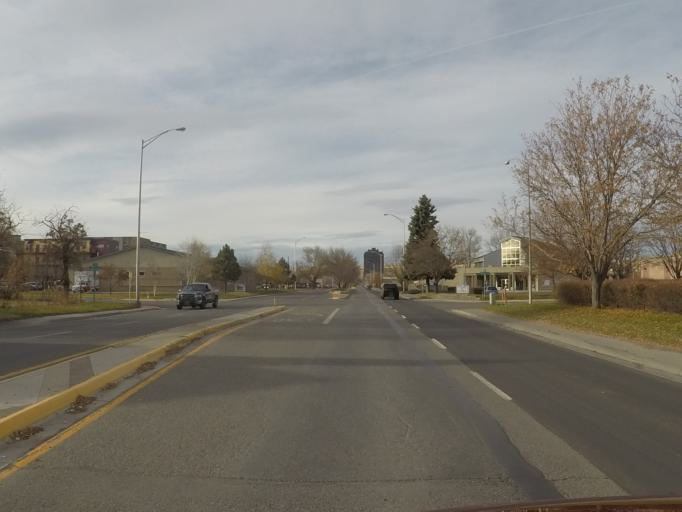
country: US
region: Montana
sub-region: Yellowstone County
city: Billings
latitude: 45.7729
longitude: -108.4948
